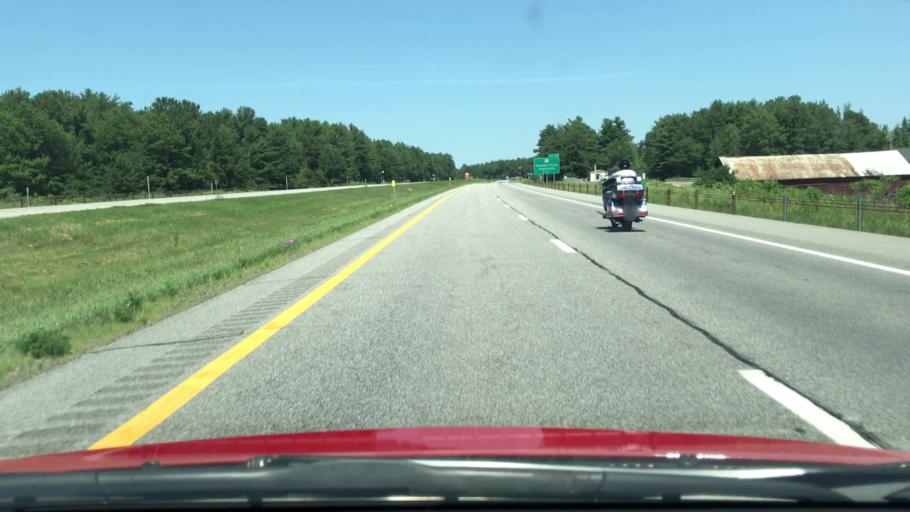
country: US
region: New York
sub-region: Essex County
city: Keeseville
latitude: 44.4789
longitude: -73.4887
